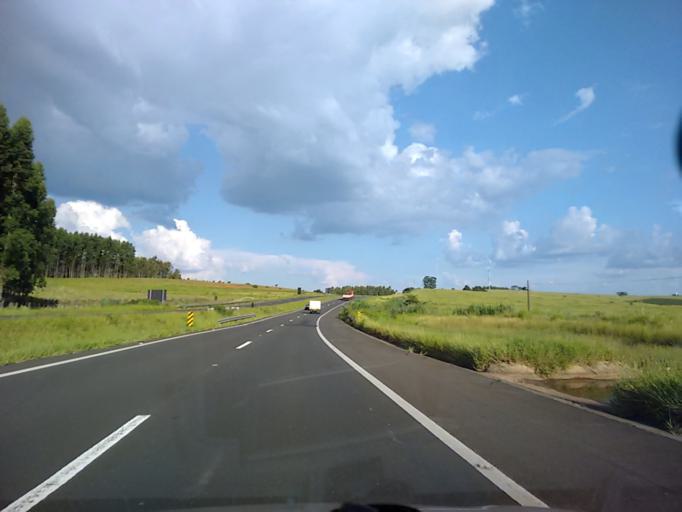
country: BR
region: Sao Paulo
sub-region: Duartina
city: Duartina
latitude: -22.3247
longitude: -49.3959
